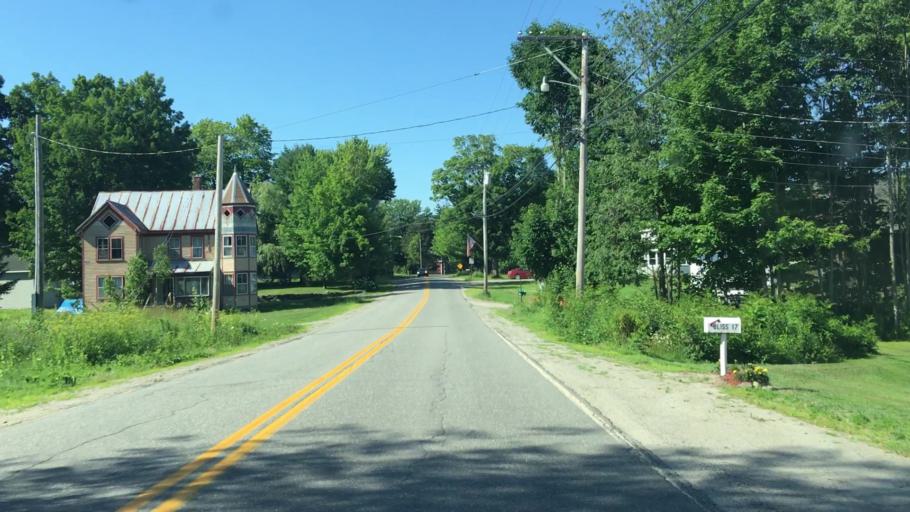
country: US
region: Maine
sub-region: Penobscot County
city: Enfield
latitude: 45.2498
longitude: -68.5657
